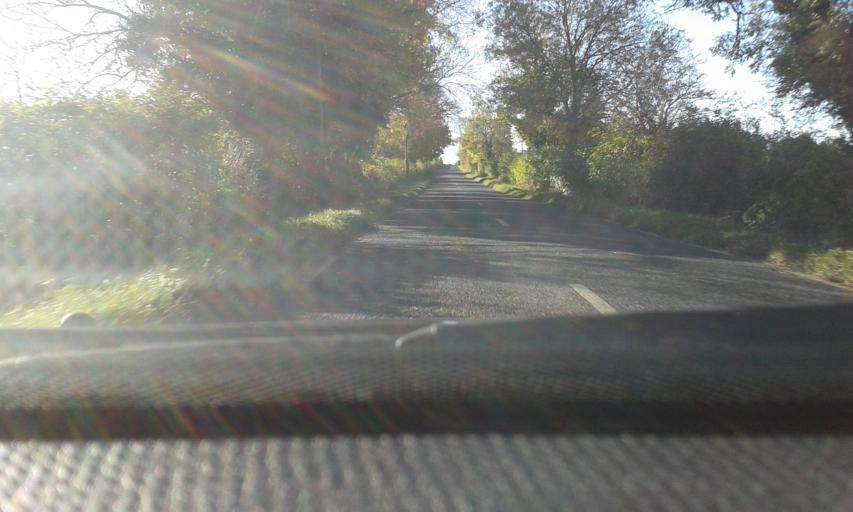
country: IE
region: Leinster
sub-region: Kildare
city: Rathangan
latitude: 53.1769
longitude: -7.0237
